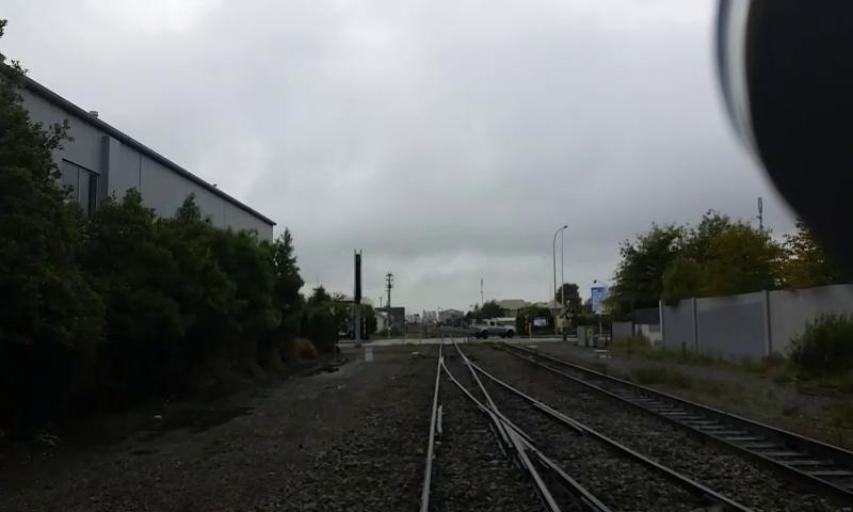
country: NZ
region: Canterbury
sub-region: Christchurch City
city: Christchurch
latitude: -43.5411
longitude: 172.6044
